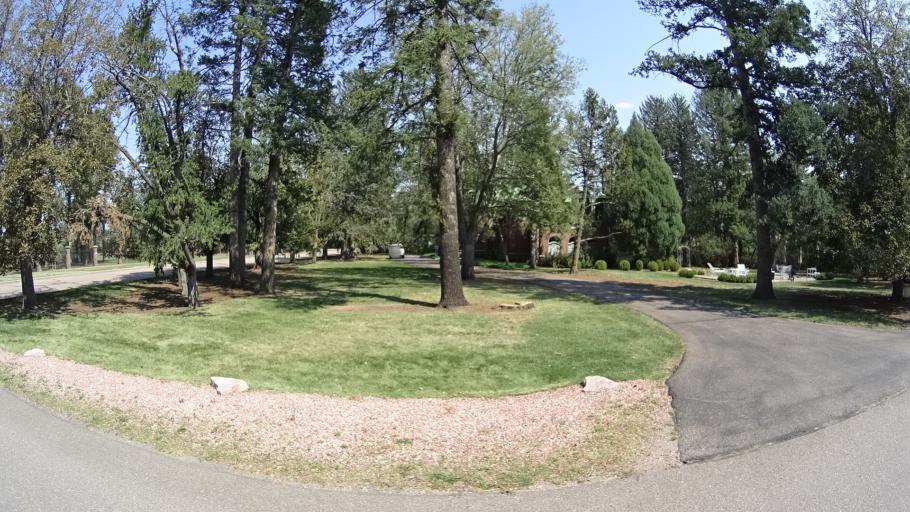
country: US
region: Colorado
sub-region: El Paso County
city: Colorado Springs
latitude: 38.7934
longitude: -104.8441
